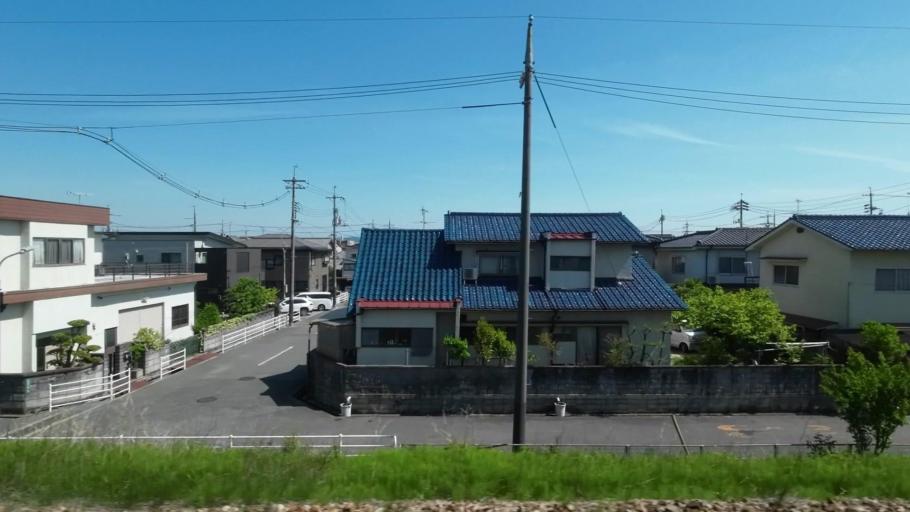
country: JP
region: Hiroshima
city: Onomichi
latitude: 34.4450
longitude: 133.2480
